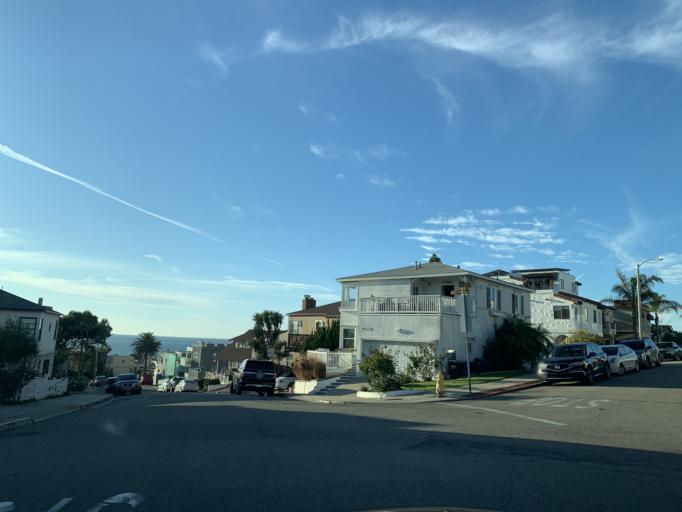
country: US
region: California
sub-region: Los Angeles County
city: Hermosa Beach
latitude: 33.8708
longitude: -118.4015
